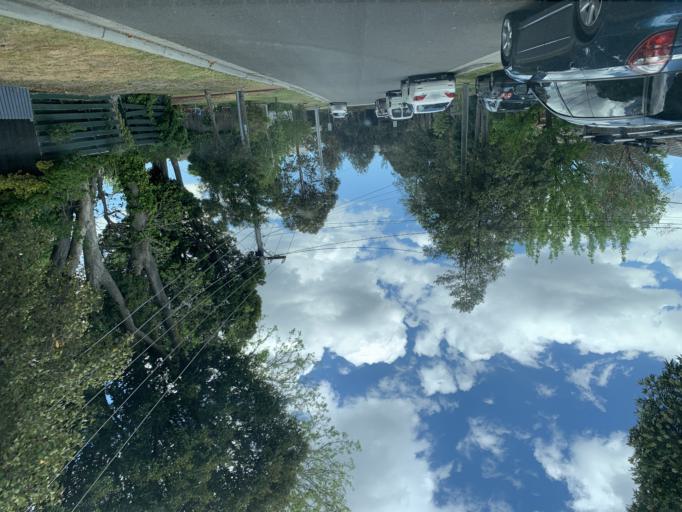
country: AU
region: Victoria
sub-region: Bayside
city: Cheltenham
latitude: -37.9630
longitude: 145.0435
